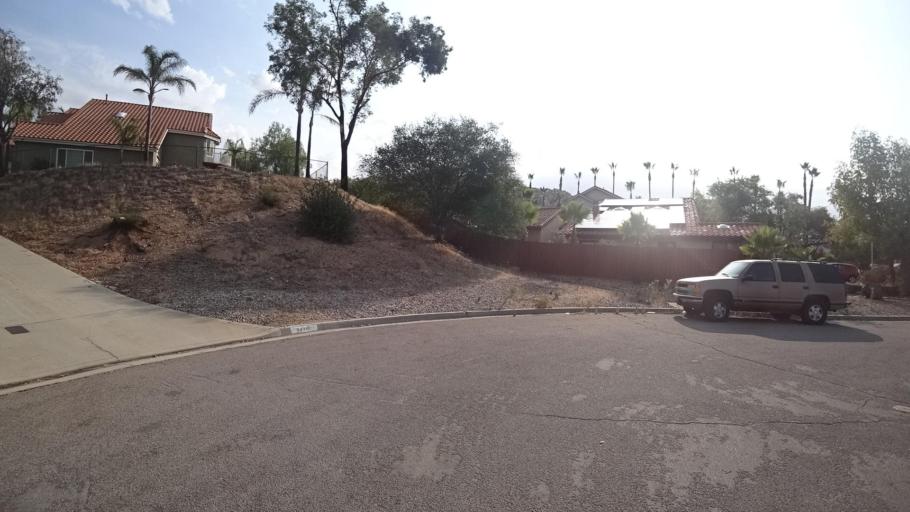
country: US
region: California
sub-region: San Diego County
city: San Diego Country Estates
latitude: 33.0143
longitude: -116.7949
